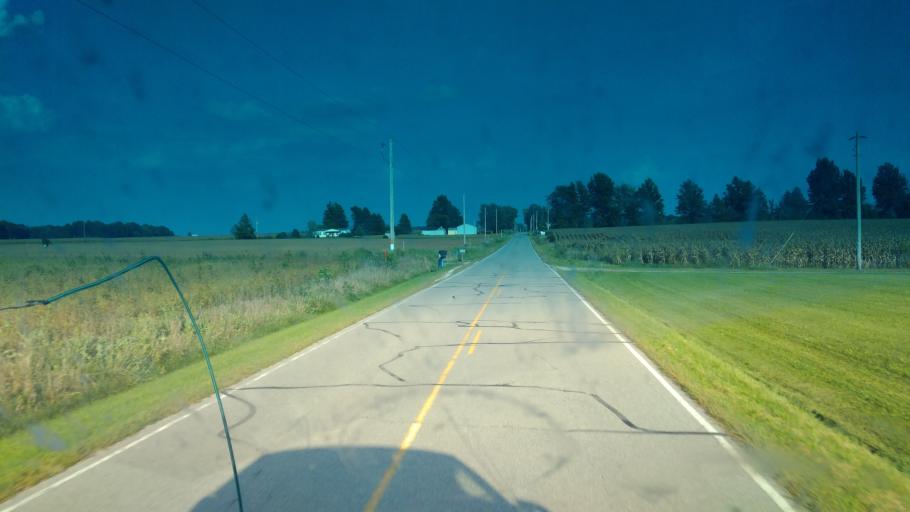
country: US
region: Ohio
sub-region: Crawford County
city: Bucyrus
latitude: 40.9650
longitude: -83.0388
